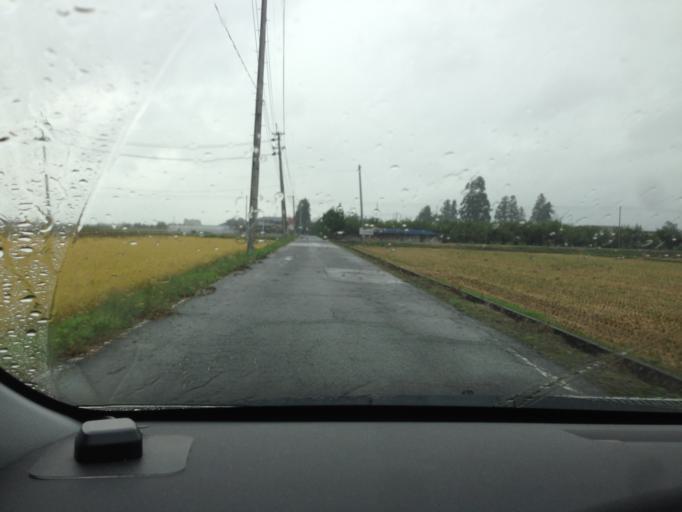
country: JP
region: Fukushima
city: Kitakata
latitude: 37.4597
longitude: 139.8711
